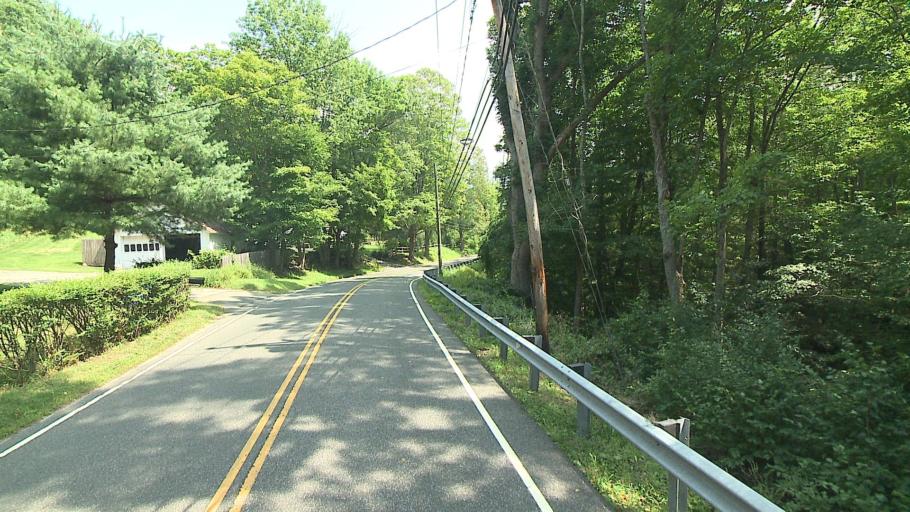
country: US
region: Connecticut
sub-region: Litchfield County
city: New Preston
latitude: 41.6497
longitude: -73.3090
